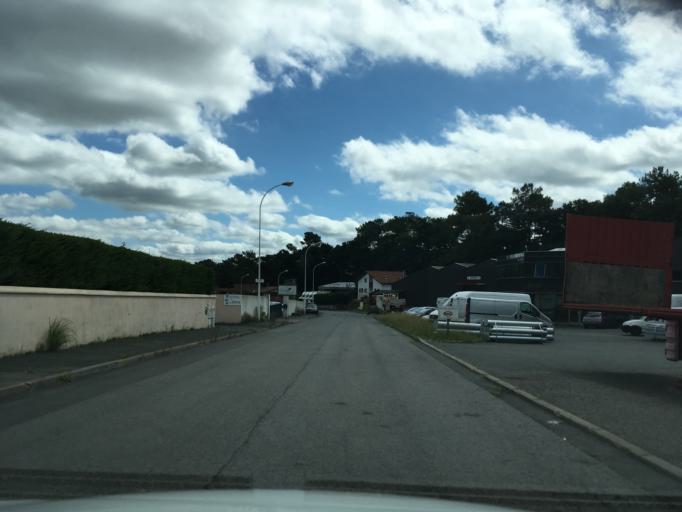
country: FR
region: Aquitaine
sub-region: Departement des Pyrenees-Atlantiques
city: Boucau
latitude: 43.5112
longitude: -1.4321
